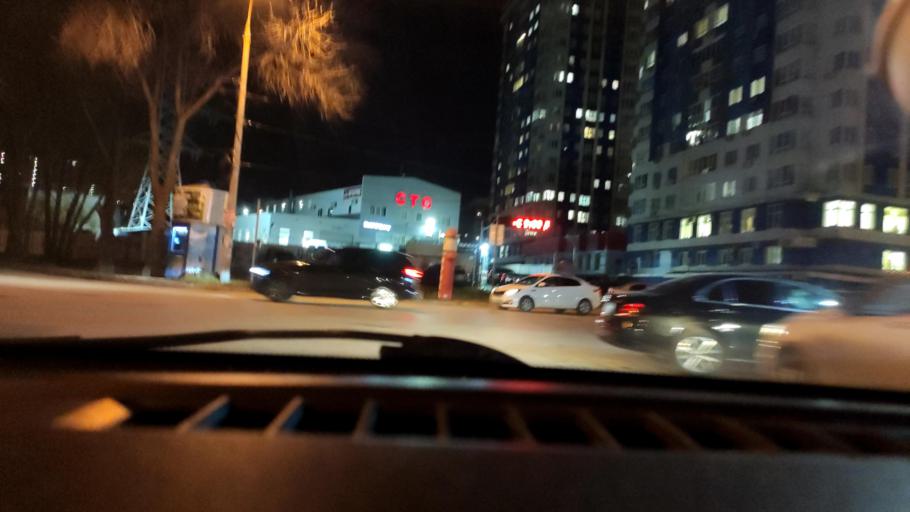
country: RU
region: Samara
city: Samara
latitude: 53.2231
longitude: 50.1530
